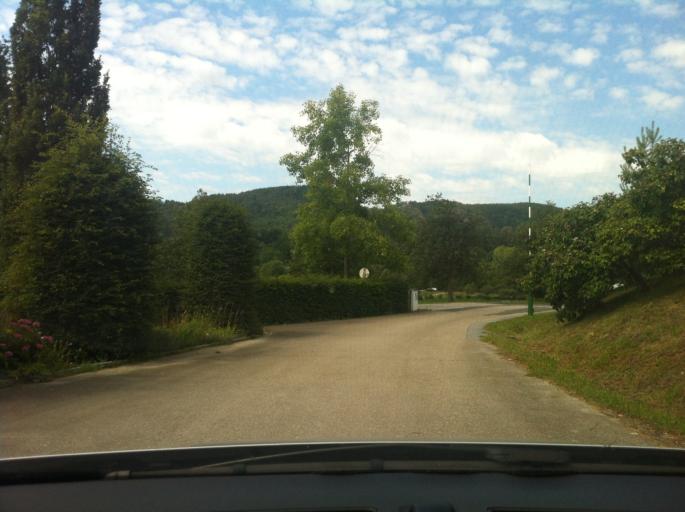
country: AT
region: Styria
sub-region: Politischer Bezirk Hartberg-Fuerstenfeld
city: Stubenberg
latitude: 47.2213
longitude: 15.8177
